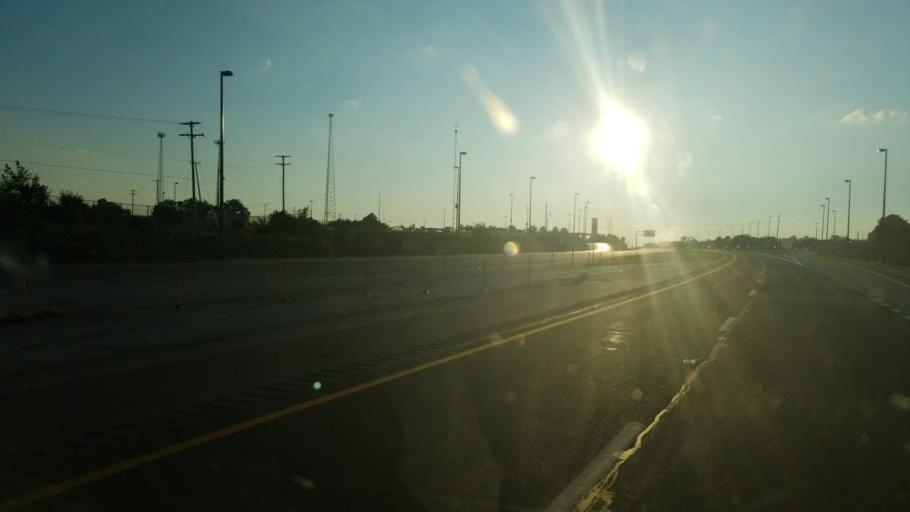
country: US
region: Ohio
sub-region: Mahoning County
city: New Middletown
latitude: 40.9384
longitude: -80.5811
